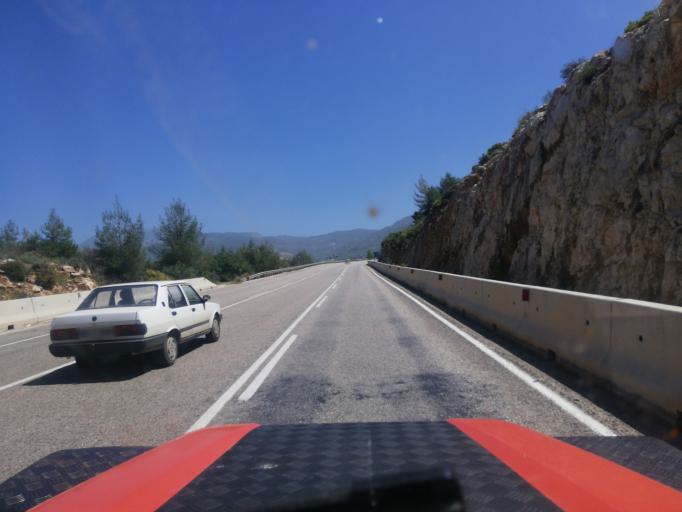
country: TR
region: Antalya
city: Kalkan
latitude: 36.2773
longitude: 29.3835
